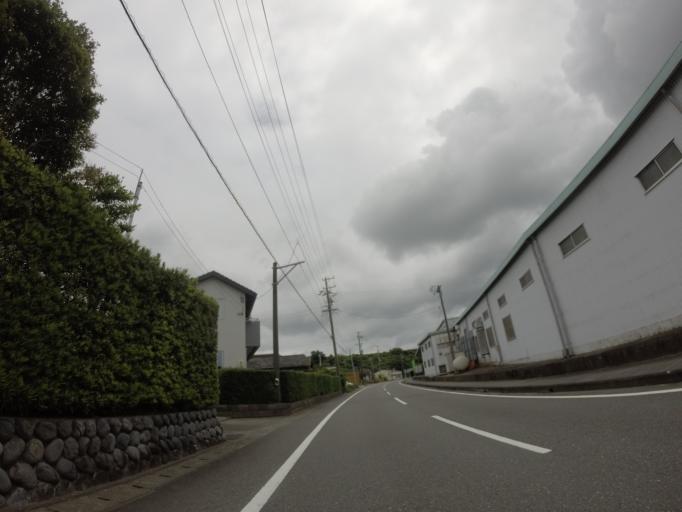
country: JP
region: Shizuoka
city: Shimada
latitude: 34.7614
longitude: 138.2006
